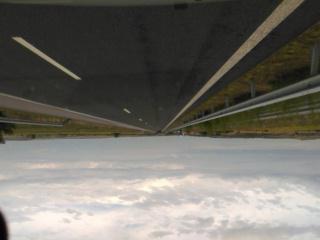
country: BG
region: Sliven
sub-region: Obshtina Sliven
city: Kermen
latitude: 42.5061
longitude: 26.3247
